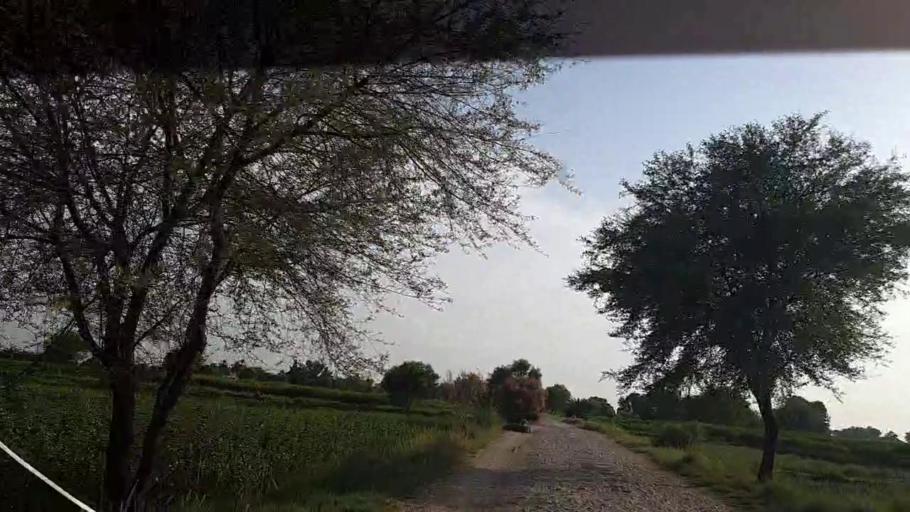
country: PK
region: Sindh
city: Khanpur
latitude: 27.8217
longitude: 69.3410
